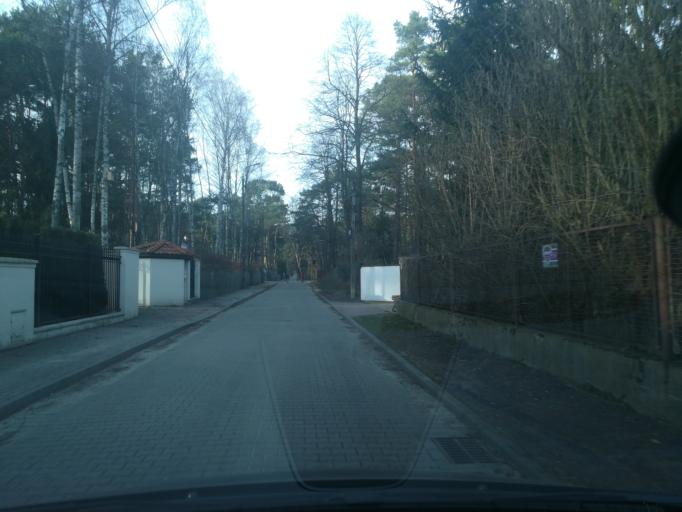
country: PL
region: Masovian Voivodeship
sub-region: Powiat piaseczynski
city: Konstancin-Jeziorna
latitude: 52.0733
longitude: 21.1044
